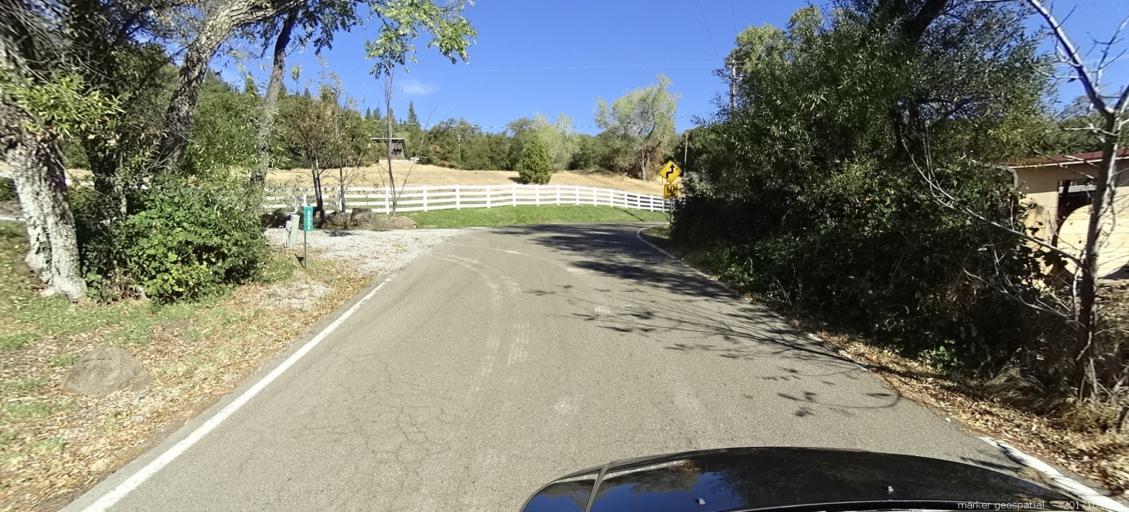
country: US
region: California
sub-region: Shasta County
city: Shingletown
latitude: 40.4621
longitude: -121.8897
